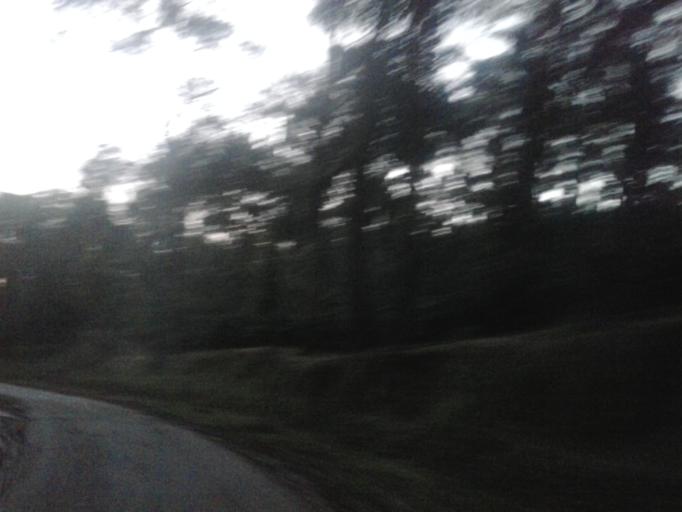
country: IN
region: Karnataka
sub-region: Hassan
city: Sakleshpur
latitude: 13.0008
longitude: 75.6857
